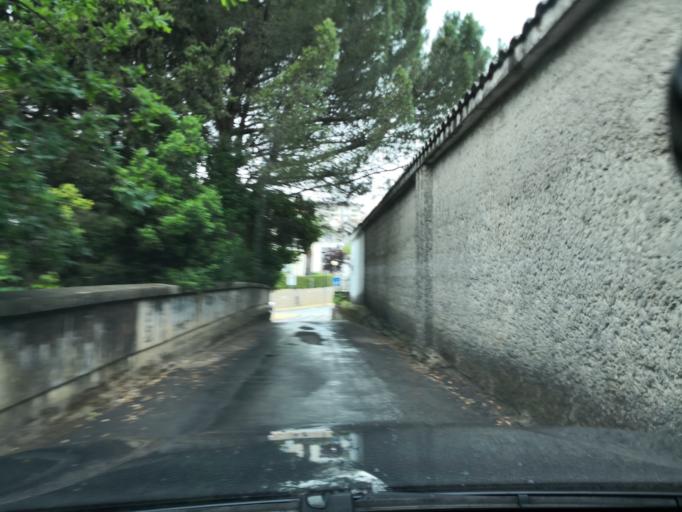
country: PT
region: Vila Real
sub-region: Vila Real
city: Vila Real
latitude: 41.3029
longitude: -7.7372
